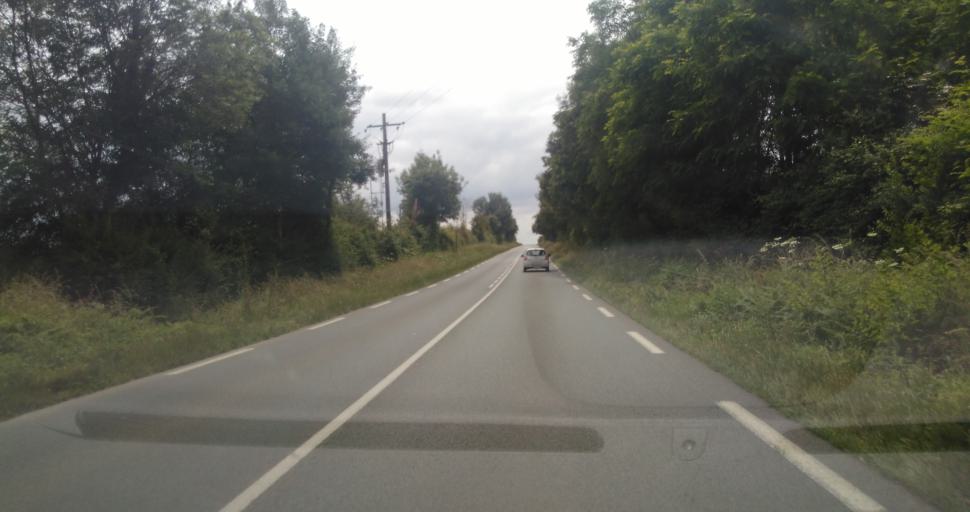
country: FR
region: Pays de la Loire
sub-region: Departement de la Vendee
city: Bournezeau
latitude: 46.6249
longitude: -1.1590
